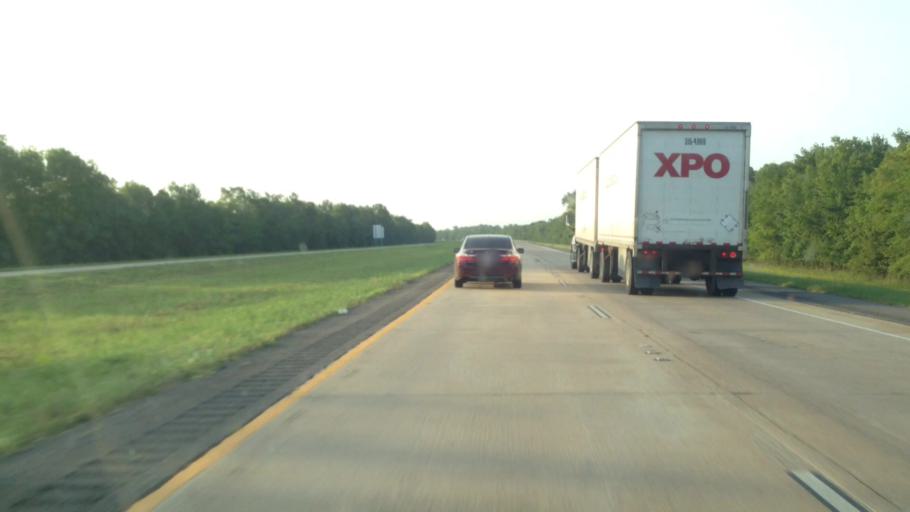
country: US
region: Louisiana
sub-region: Natchitoches Parish
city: Vienna Bend
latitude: 31.5823
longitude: -93.0258
